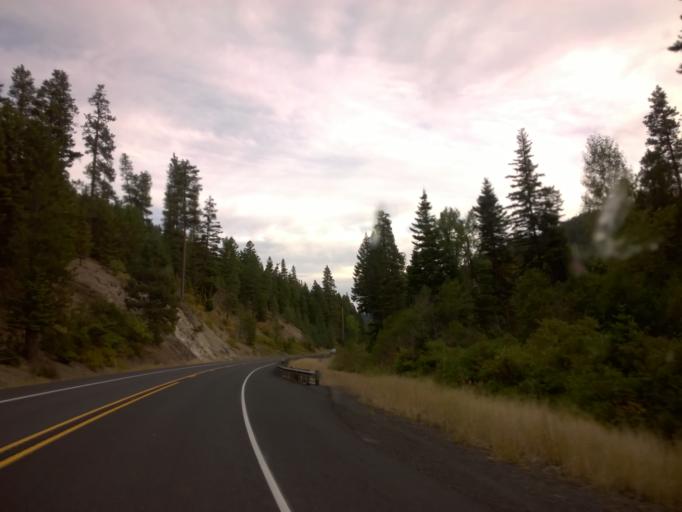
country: US
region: Washington
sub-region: Kittitas County
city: Cle Elum
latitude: 47.2873
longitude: -120.6973
